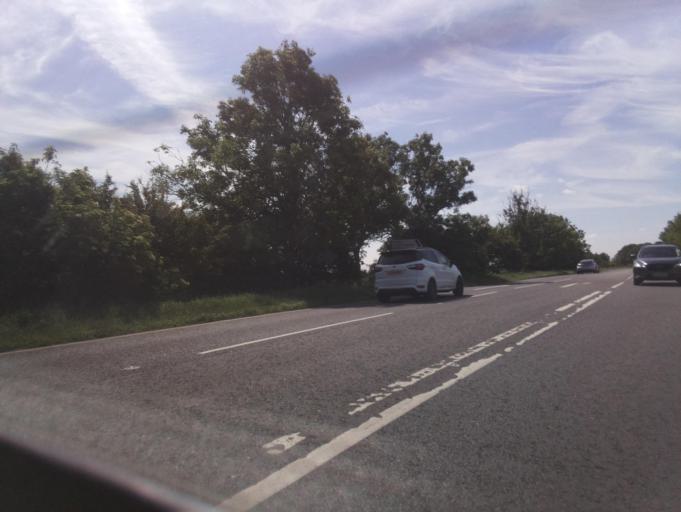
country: GB
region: England
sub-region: Lincolnshire
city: Burton
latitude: 53.3352
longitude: -0.5438
